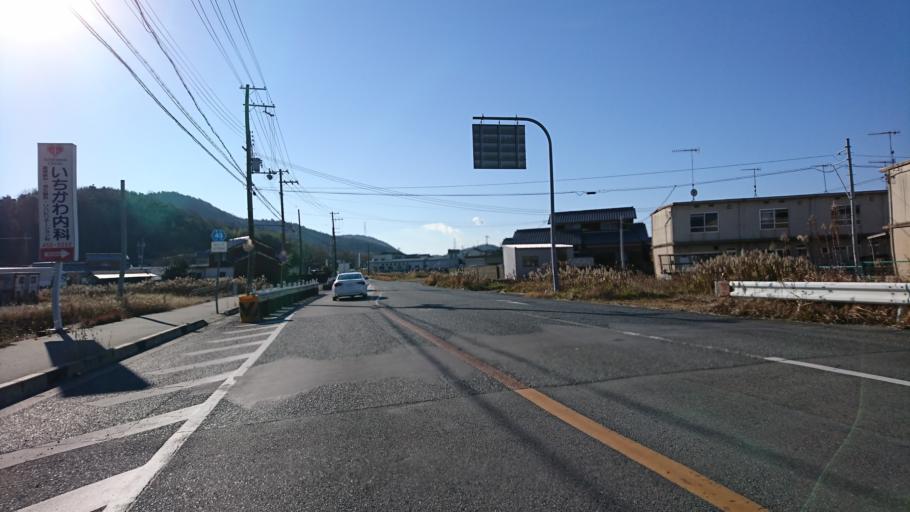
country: JP
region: Hyogo
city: Kakogawacho-honmachi
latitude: 34.8143
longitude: 134.8359
